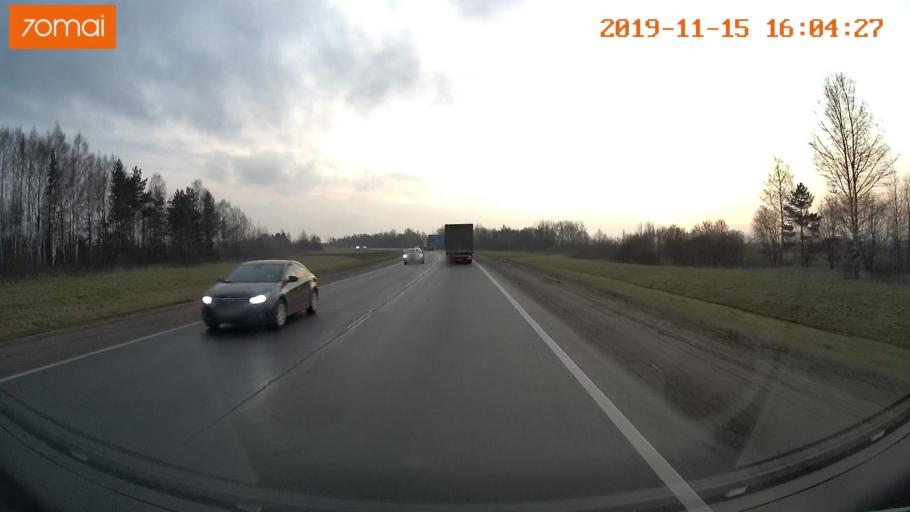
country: RU
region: Jaroslavl
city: Yaroslavl
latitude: 57.7478
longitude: 39.9013
